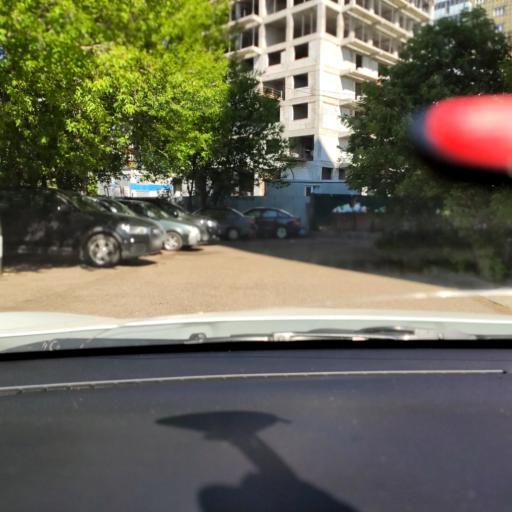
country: RU
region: Tatarstan
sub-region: Gorod Kazan'
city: Kazan
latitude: 55.8043
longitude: 49.1730
